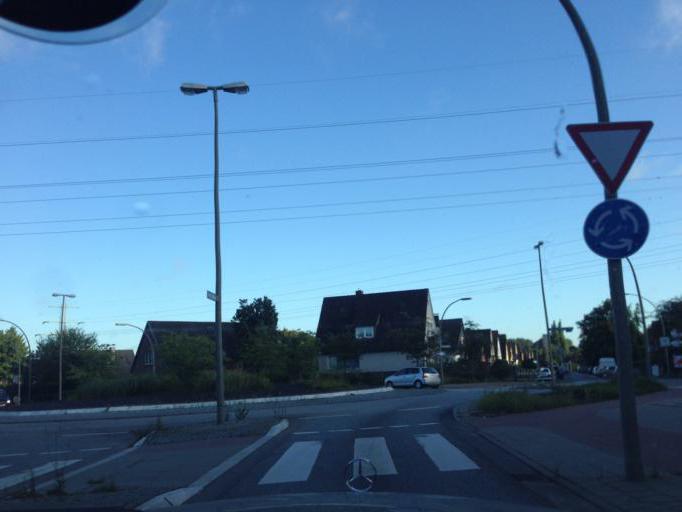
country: DE
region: Hamburg
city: Farmsen-Berne
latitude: 53.5932
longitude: 10.0981
